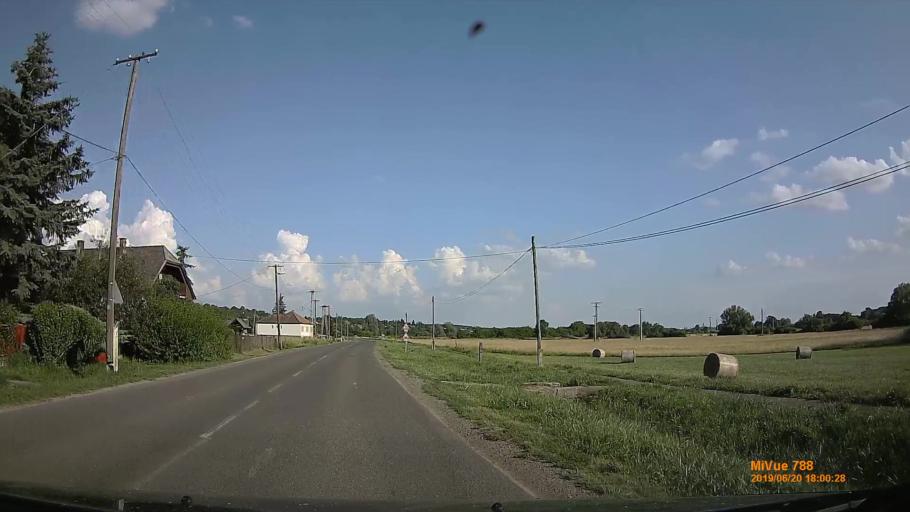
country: HU
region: Baranya
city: Buekkoesd
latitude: 46.0885
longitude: 17.9816
